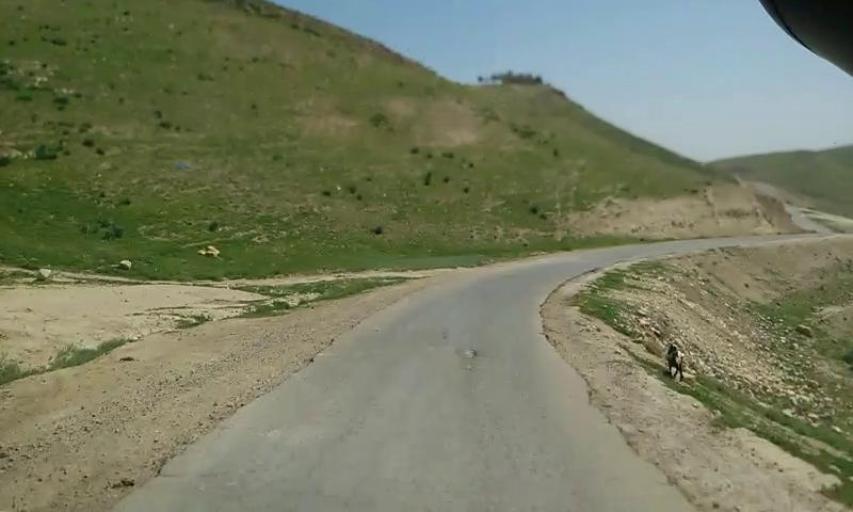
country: PS
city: `Arab ar Rashaydah
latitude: 31.5646
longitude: 35.2404
